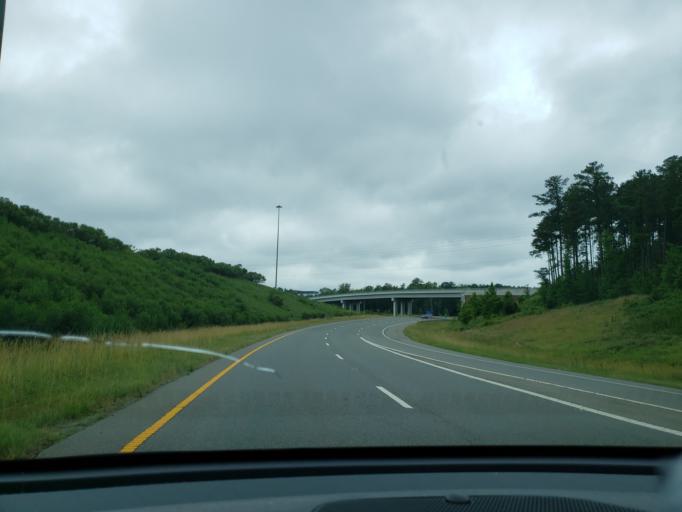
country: US
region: North Carolina
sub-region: Wake County
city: Morrisville
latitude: 35.8572
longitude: -78.8606
